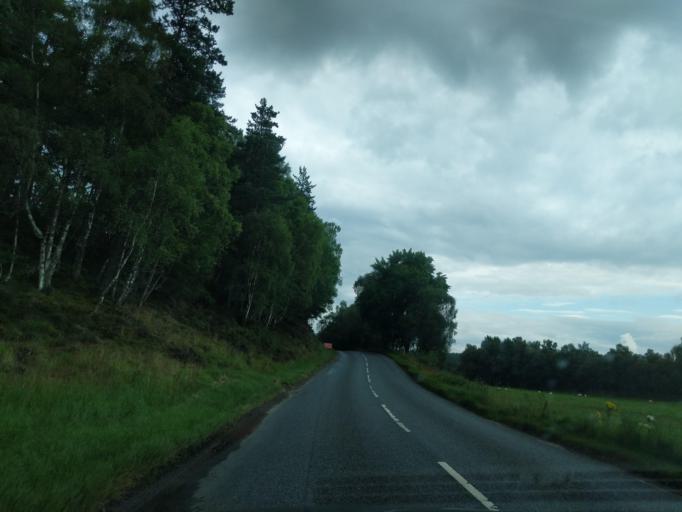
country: GB
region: Scotland
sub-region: Highland
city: Aviemore
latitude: 57.2935
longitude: -3.7903
